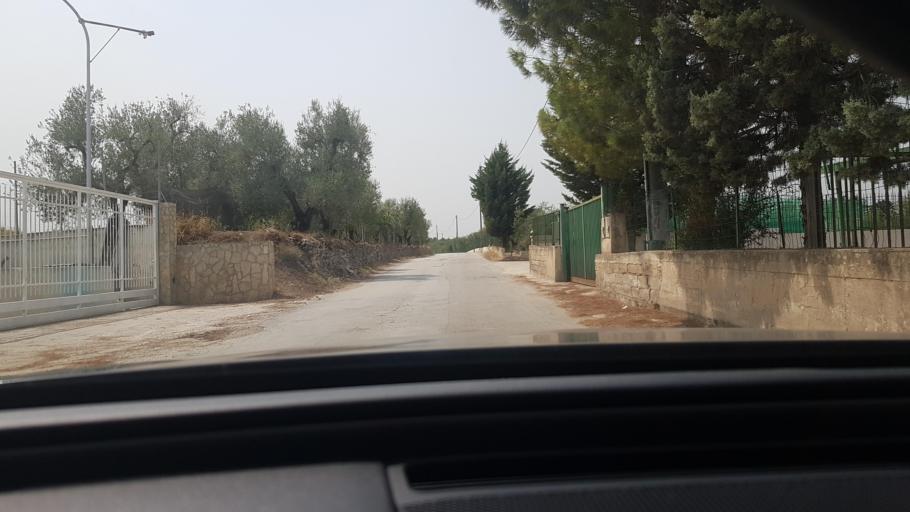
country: IT
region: Apulia
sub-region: Provincia di Barletta - Andria - Trani
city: Andria
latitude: 41.2241
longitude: 16.2666
